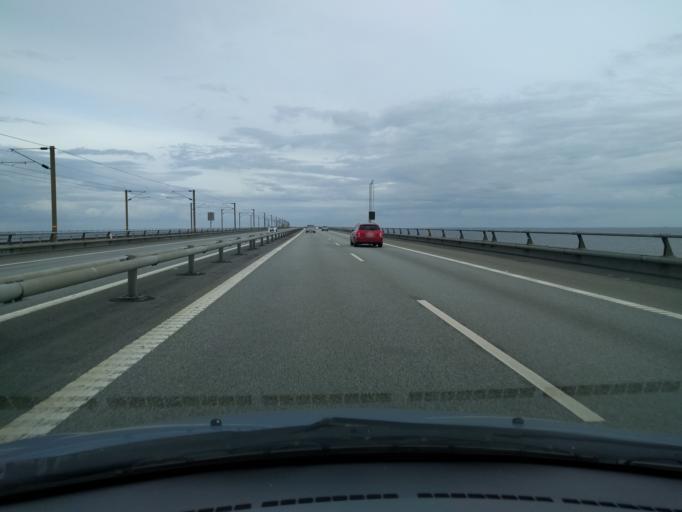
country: DK
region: South Denmark
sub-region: Nyborg Kommune
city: Nyborg
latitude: 55.3012
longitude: 10.8627
